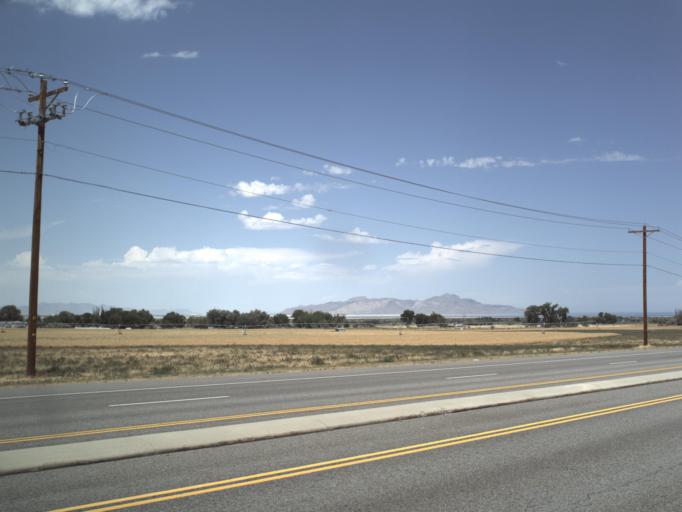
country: US
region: Utah
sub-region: Tooele County
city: Erda
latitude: 40.6011
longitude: -112.2941
